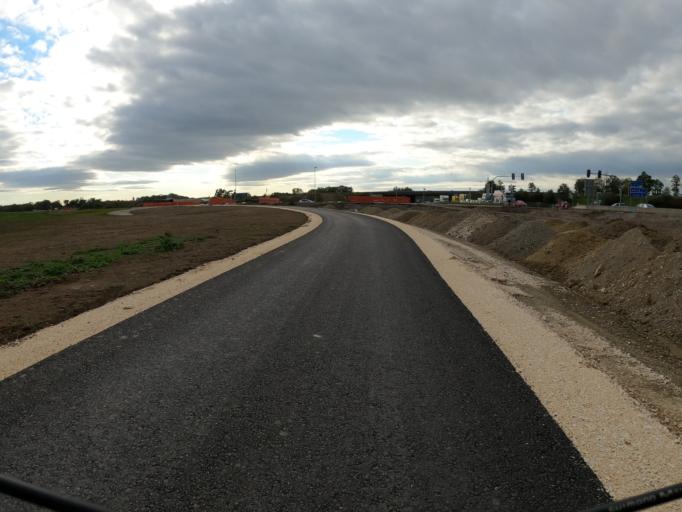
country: DE
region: Bavaria
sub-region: Swabia
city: Nersingen
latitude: 48.4144
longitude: 10.0975
